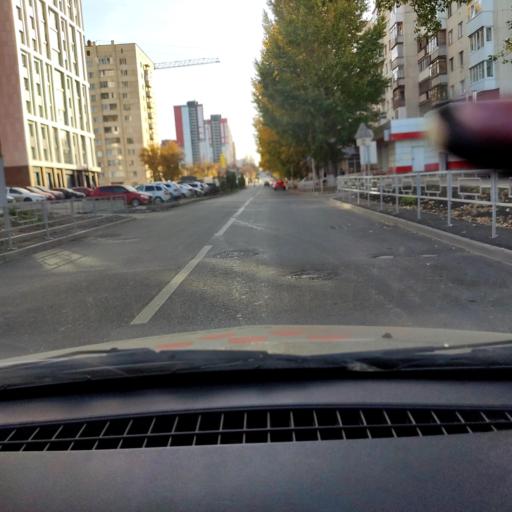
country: RU
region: Bashkortostan
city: Ufa
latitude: 54.7359
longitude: 55.9329
